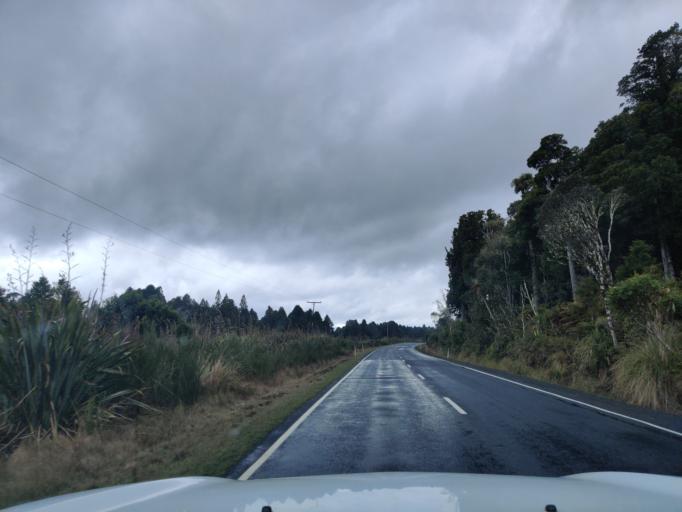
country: NZ
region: Manawatu-Wanganui
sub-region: Ruapehu District
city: Waiouru
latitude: -39.2488
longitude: 175.3887
